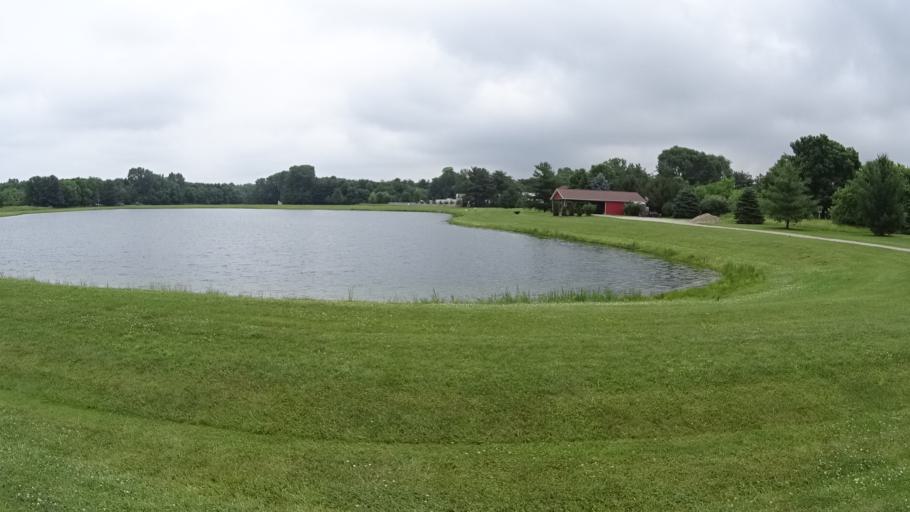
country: US
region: Ohio
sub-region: Erie County
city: Milan
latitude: 41.3011
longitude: -82.5586
